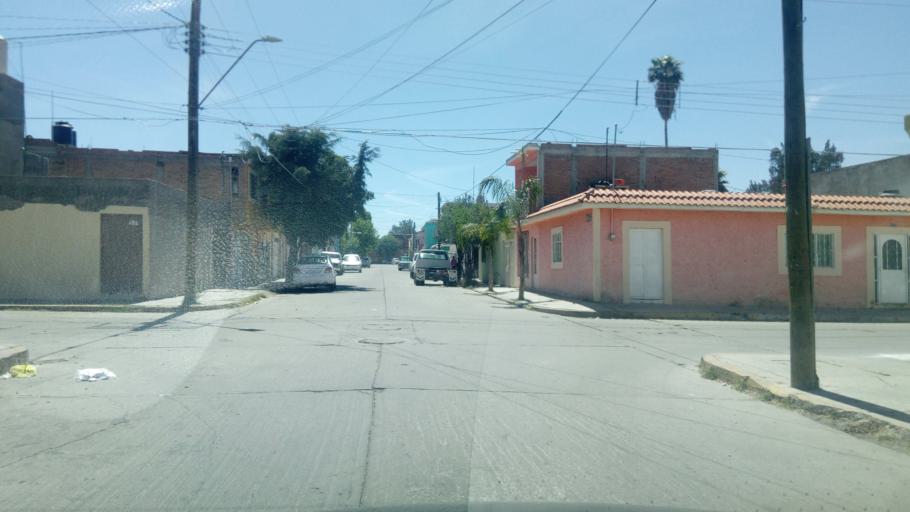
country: MX
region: Durango
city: Victoria de Durango
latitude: 24.0110
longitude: -104.6582
